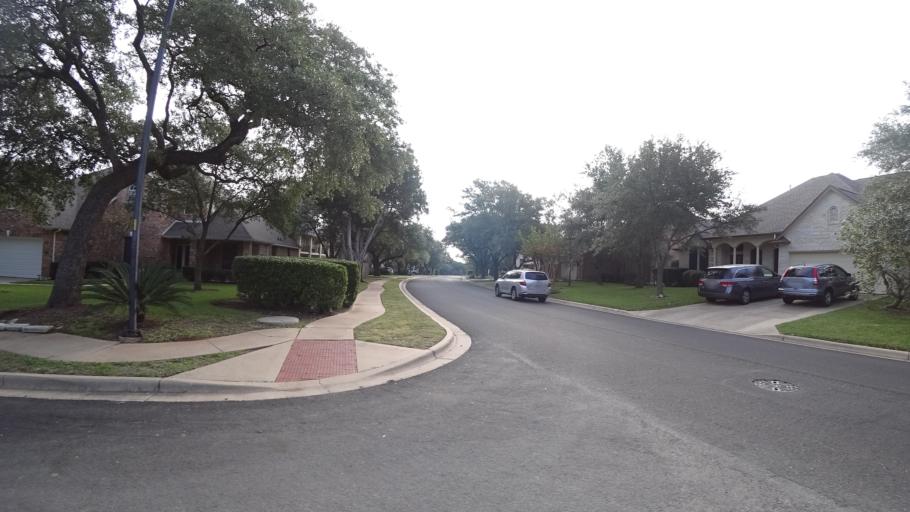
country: US
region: Texas
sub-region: Travis County
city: Shady Hollow
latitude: 30.1872
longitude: -97.8844
